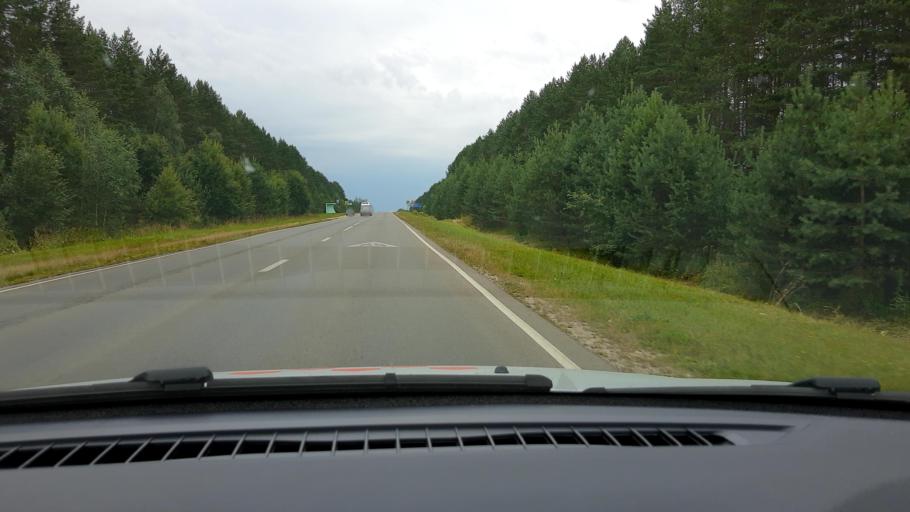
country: RU
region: Nizjnij Novgorod
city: Vyyezdnoye
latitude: 55.1572
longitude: 43.5777
